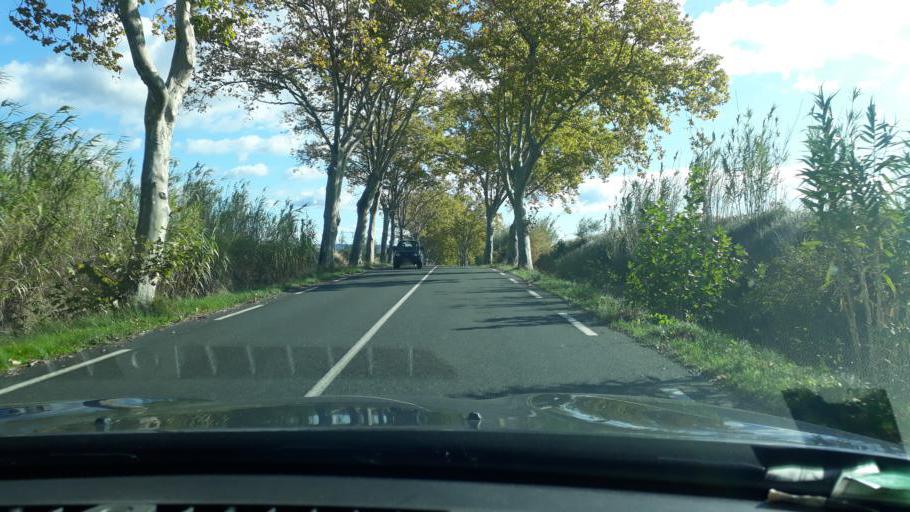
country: FR
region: Languedoc-Roussillon
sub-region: Departement de l'Herault
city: Saint-Andre-de-Sangonis
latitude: 43.6520
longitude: 3.4938
